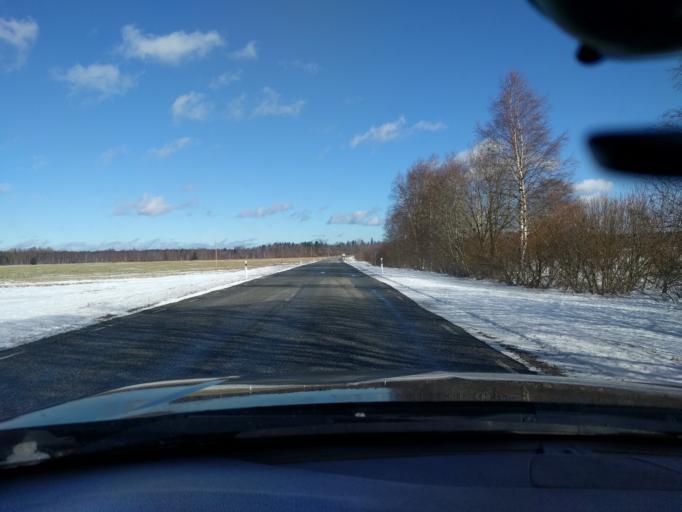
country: EE
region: Harju
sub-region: Raasiku vald
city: Raasiku
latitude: 59.4029
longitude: 25.2033
